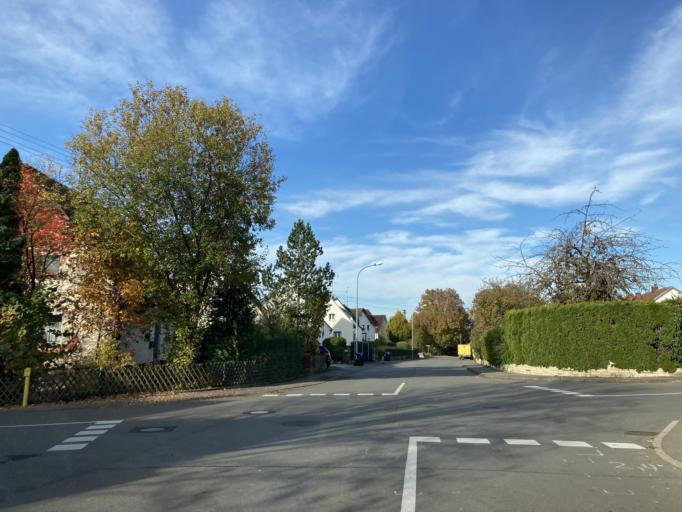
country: DE
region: Baden-Wuerttemberg
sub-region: Tuebingen Region
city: Bodelshausen
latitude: 48.3968
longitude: 8.9769
